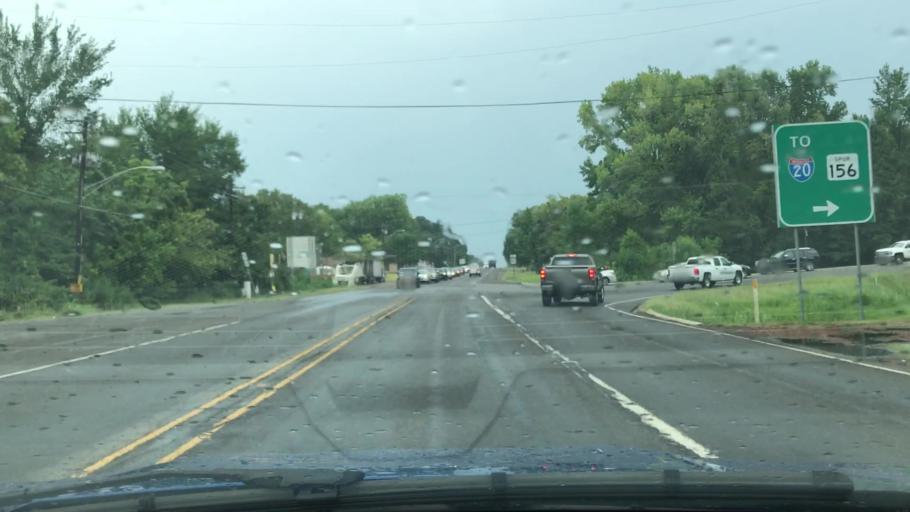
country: US
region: Texas
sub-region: Harrison County
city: Waskom
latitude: 32.4766
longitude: -94.0529
